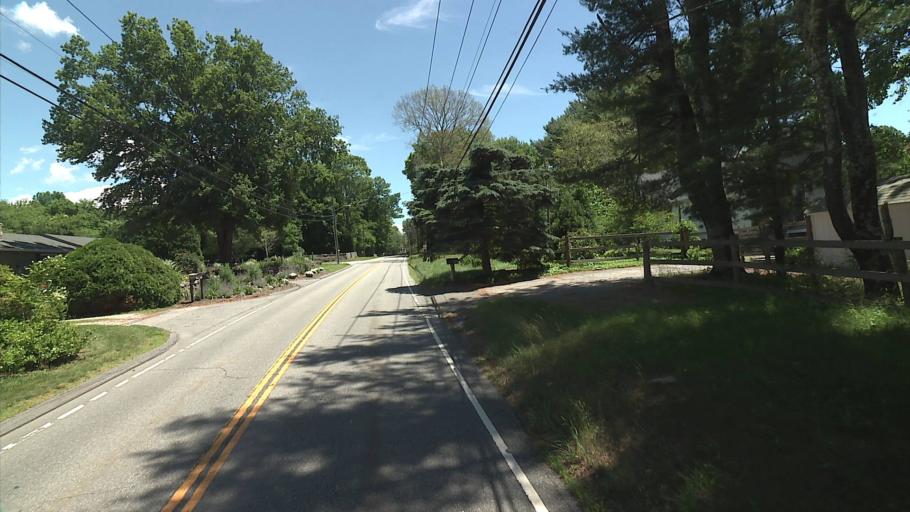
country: US
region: Connecticut
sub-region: New London County
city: Pawcatuck
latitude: 41.3836
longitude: -71.8652
